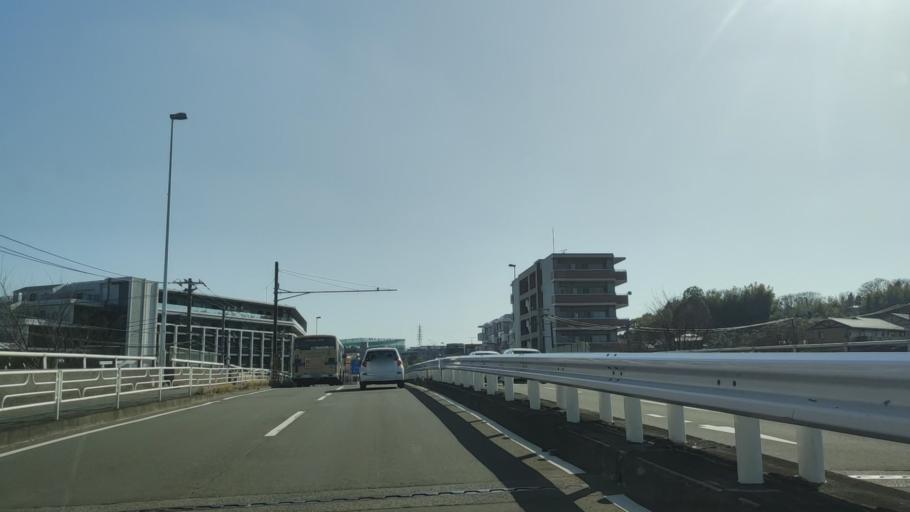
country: JP
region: Kanagawa
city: Yokohama
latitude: 35.4939
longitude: 139.6074
